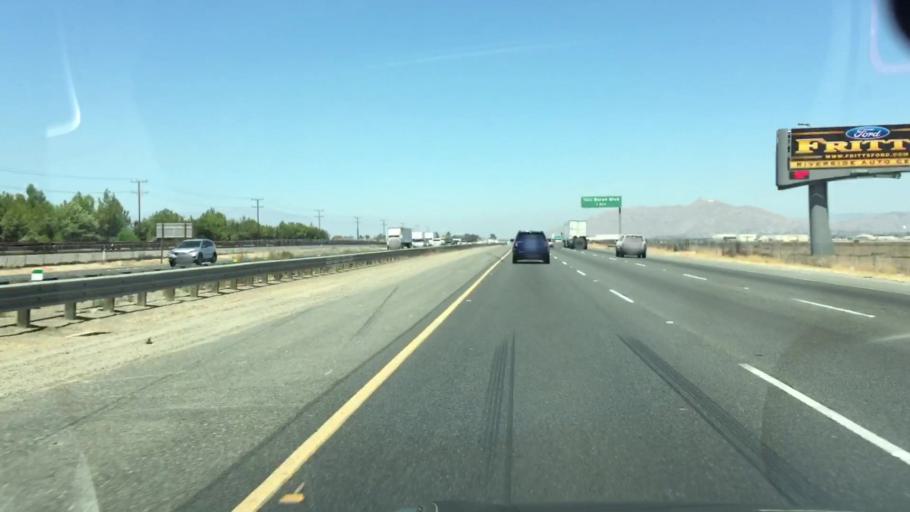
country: US
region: California
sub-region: Riverside County
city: March Air Force Base
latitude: 33.8690
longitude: -117.2622
